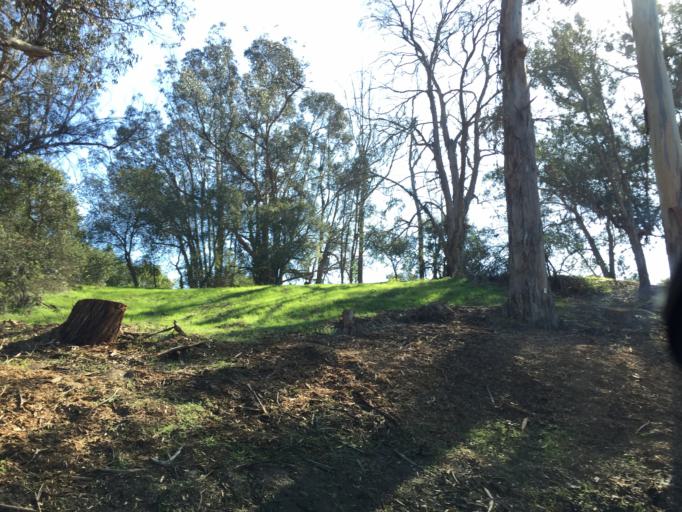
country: US
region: California
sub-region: Santa Barbara County
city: Goleta
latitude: 34.4294
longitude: -119.7763
